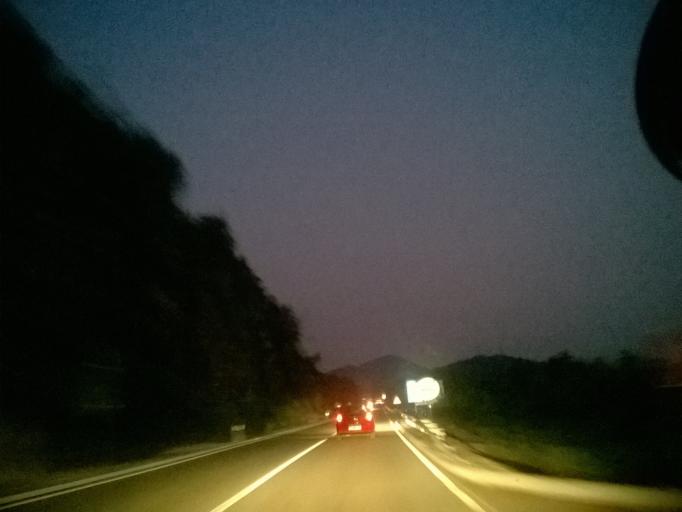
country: ME
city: Mojanovici
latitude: 42.3850
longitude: 19.0909
